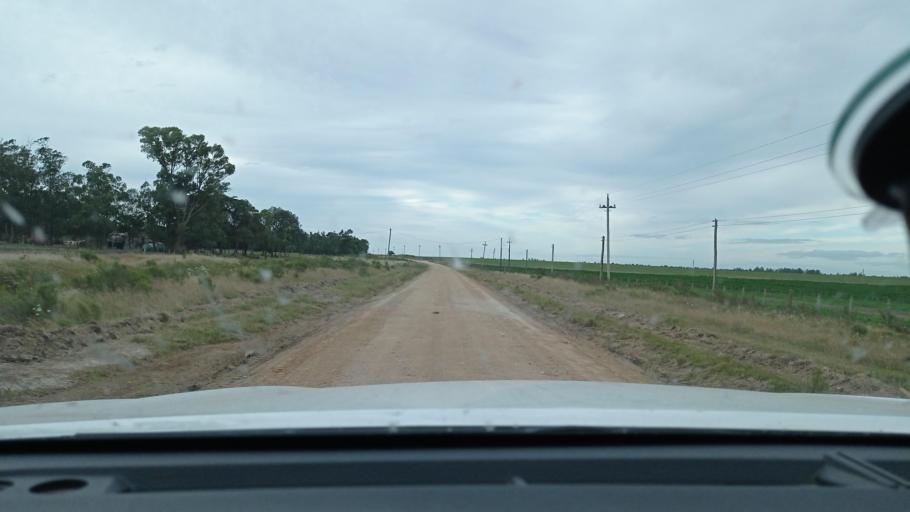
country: UY
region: Florida
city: Casupa
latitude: -34.1123
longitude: -55.7662
